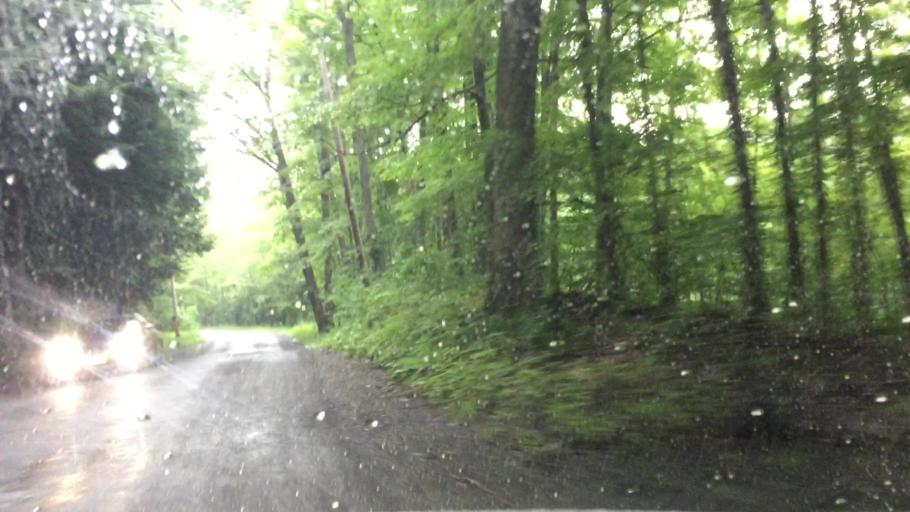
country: US
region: Massachusetts
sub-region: Berkshire County
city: Housatonic
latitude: 42.2992
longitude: -73.3821
